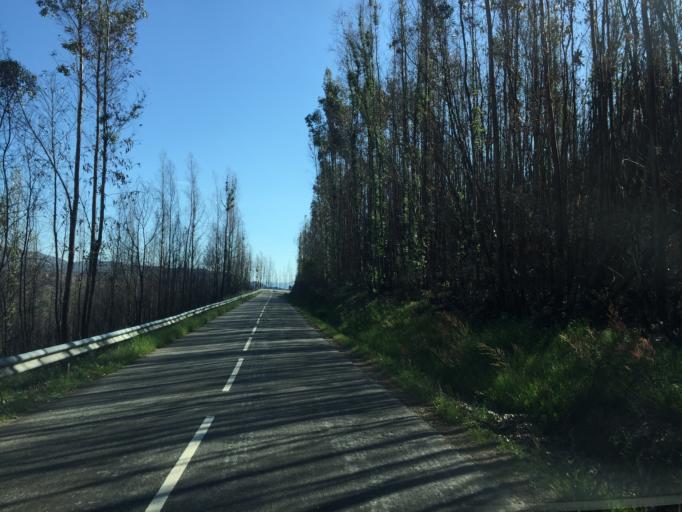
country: PT
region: Coimbra
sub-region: Pampilhosa da Serra
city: Pampilhosa da Serra
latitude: 40.0407
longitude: -7.9098
